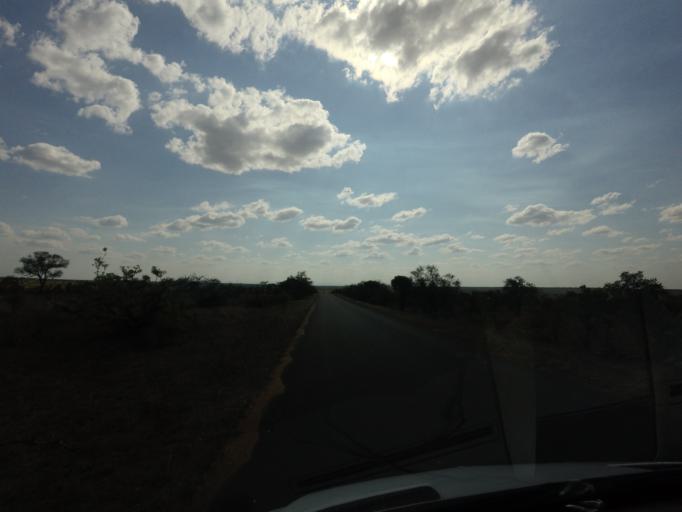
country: ZA
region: Limpopo
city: Thulamahashi
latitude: -24.3943
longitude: 31.5985
